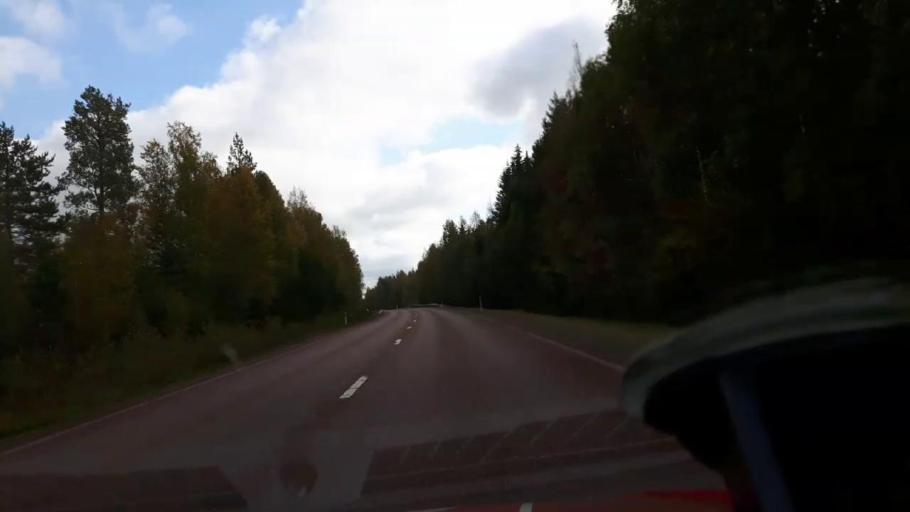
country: SE
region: Gaevleborg
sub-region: Ljusdals Kommun
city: Jaervsoe
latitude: 61.6382
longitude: 16.2423
